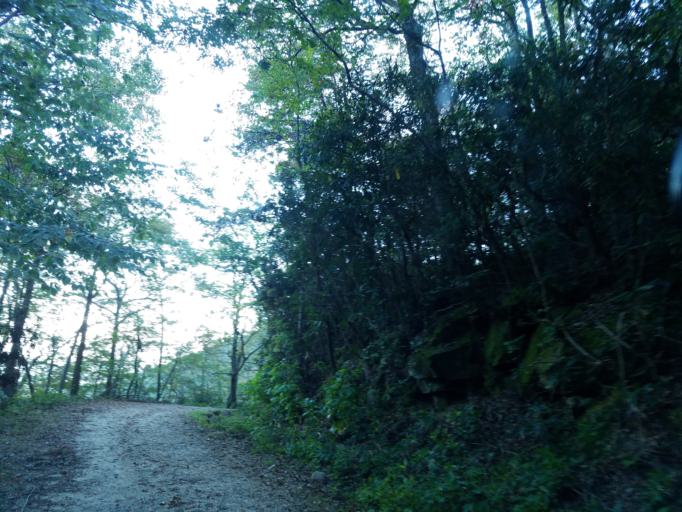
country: US
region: Georgia
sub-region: Dawson County
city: Dawsonville
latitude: 34.5991
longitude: -84.2114
